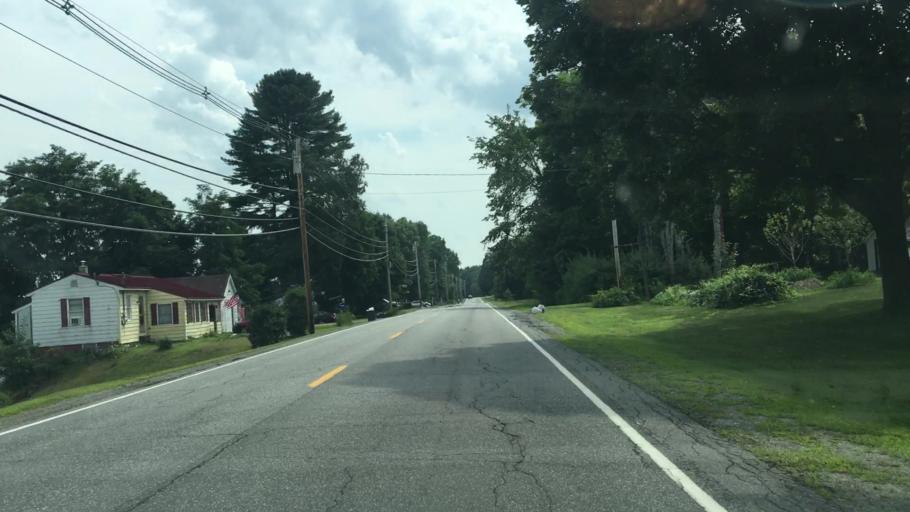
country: US
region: Maine
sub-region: Kennebec County
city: Winslow
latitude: 44.5049
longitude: -69.6327
